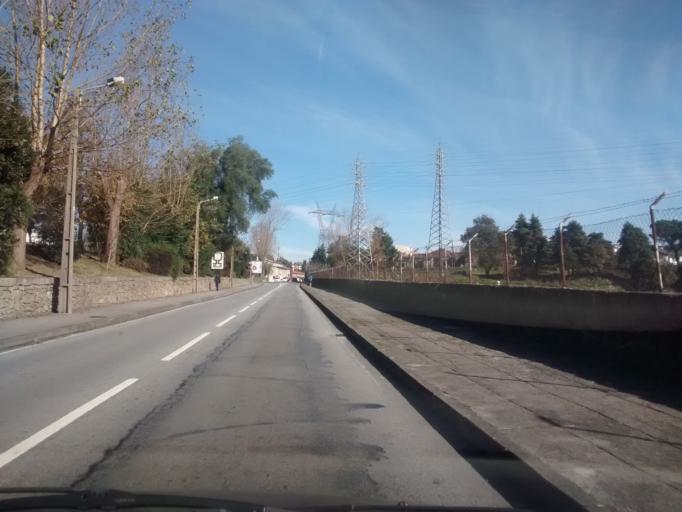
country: PT
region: Braga
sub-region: Braga
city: Braga
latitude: 41.5594
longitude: -8.3960
